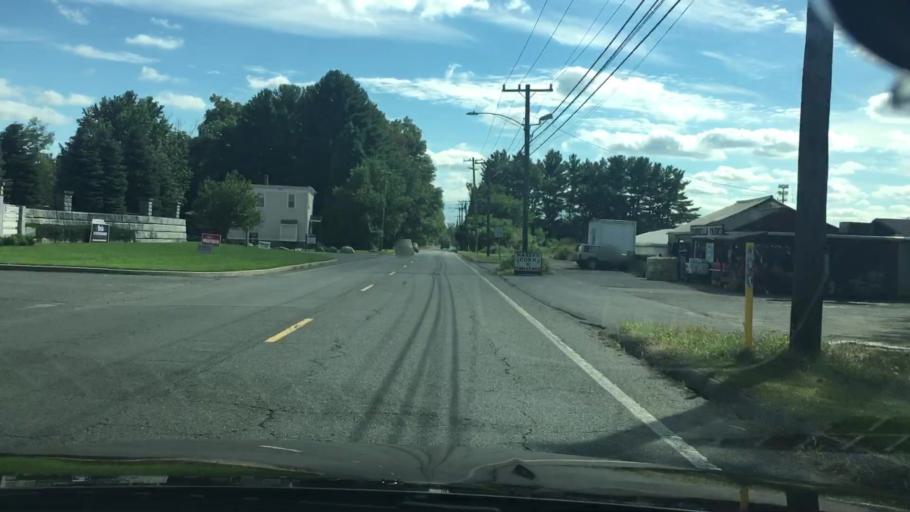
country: US
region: Connecticut
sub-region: Hartford County
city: Plainville
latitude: 41.6573
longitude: -72.8750
